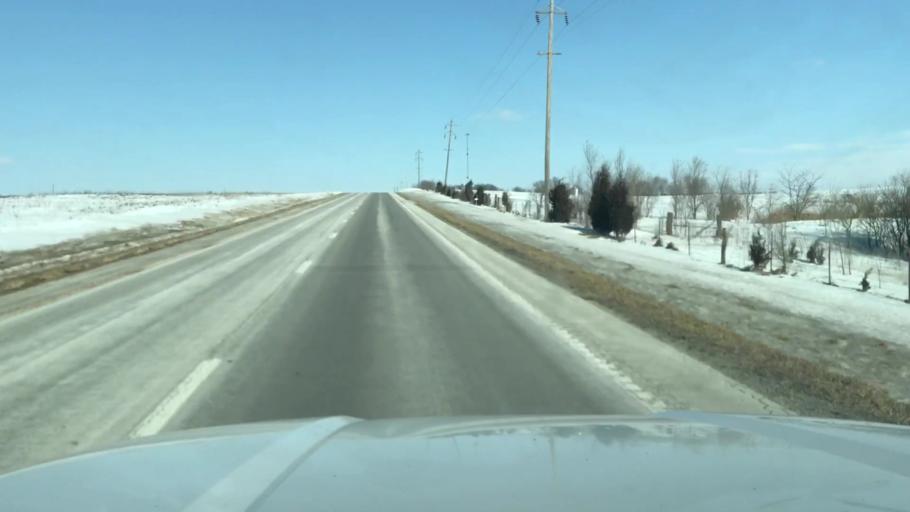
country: US
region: Missouri
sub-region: Nodaway County
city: Maryville
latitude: 40.1727
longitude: -94.8688
